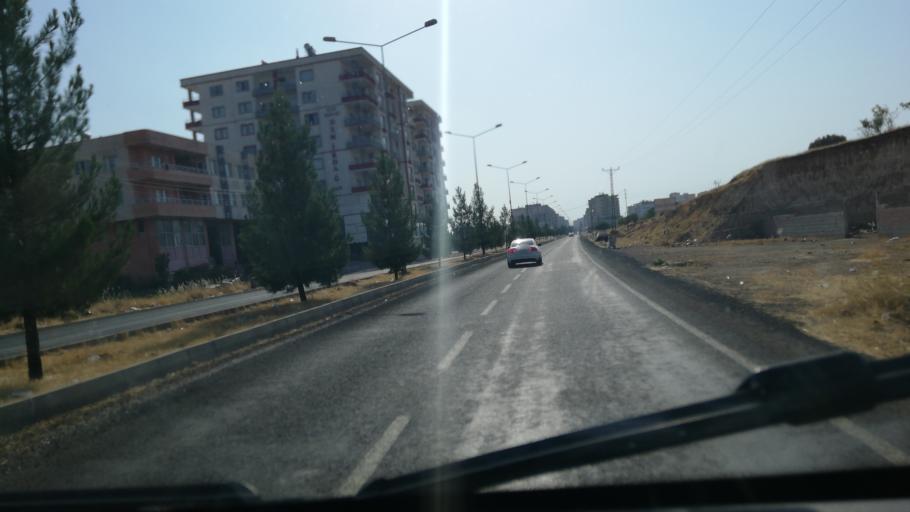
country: TR
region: Mardin
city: Midyat
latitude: 37.4364
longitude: 41.3177
